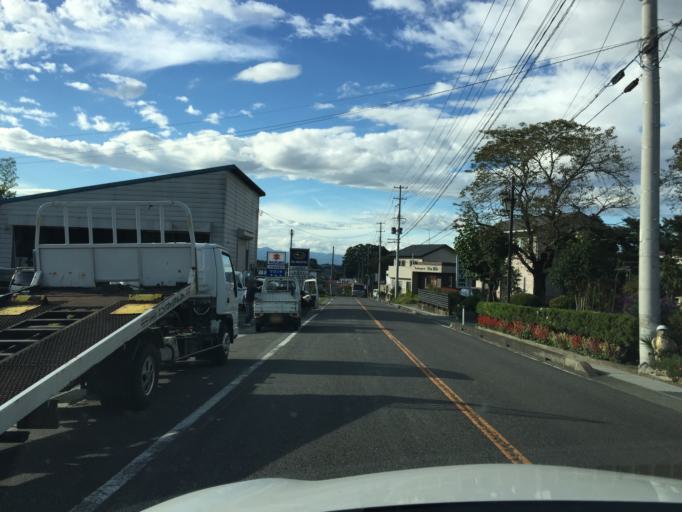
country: JP
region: Fukushima
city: Sukagawa
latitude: 37.2642
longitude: 140.4203
